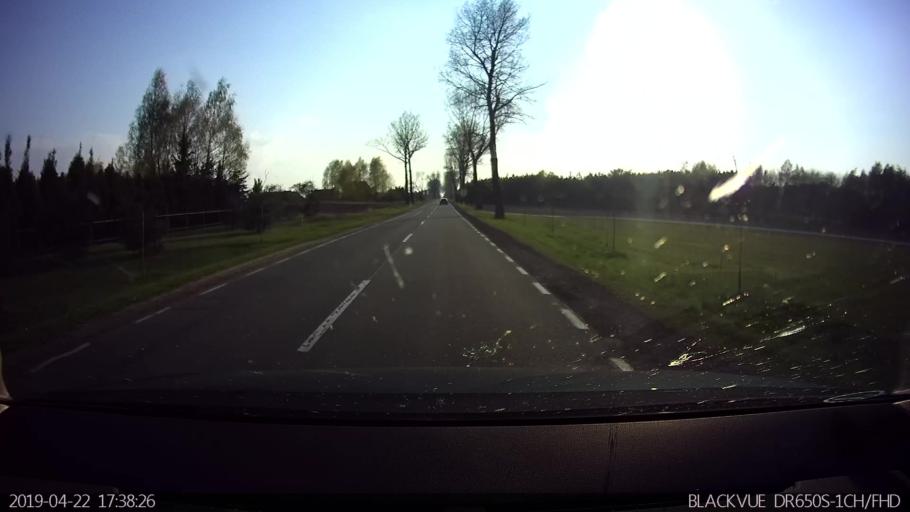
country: PL
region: Masovian Voivodeship
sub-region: Powiat sokolowski
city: Sokolow Podlaski
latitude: 52.4089
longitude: 22.1613
